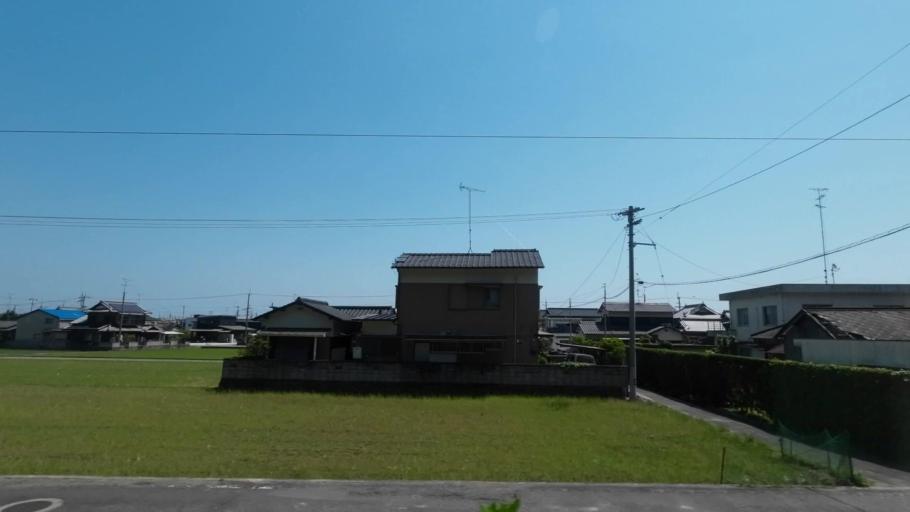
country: JP
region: Ehime
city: Saijo
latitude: 34.0149
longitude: 133.0346
